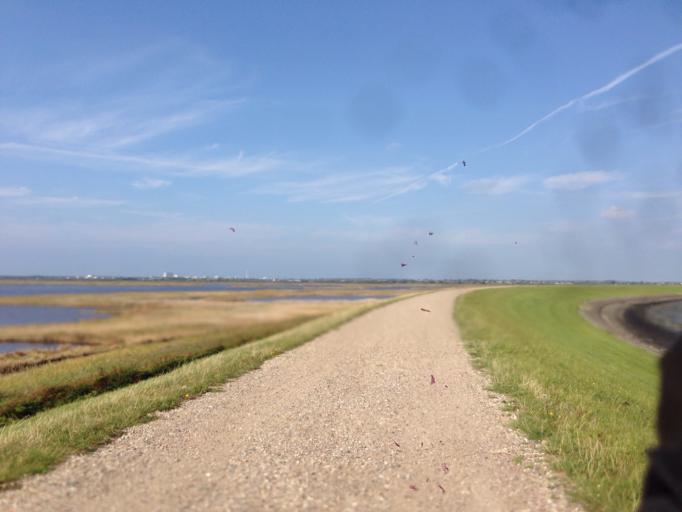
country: DE
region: Schleswig-Holstein
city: Tinnum
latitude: 54.8711
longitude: 8.3323
